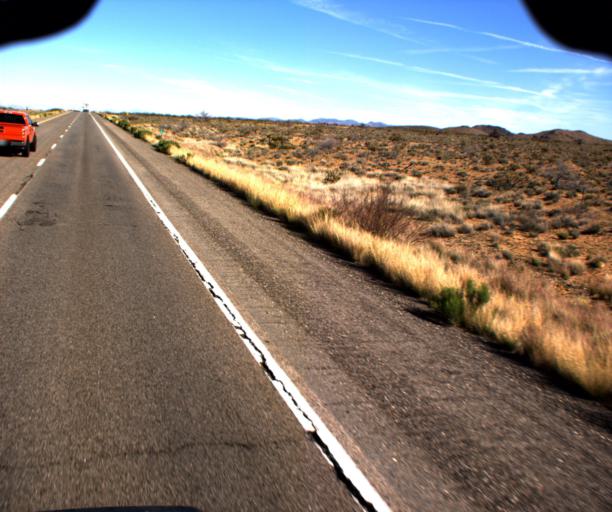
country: US
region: Arizona
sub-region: Mohave County
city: Dolan Springs
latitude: 35.4624
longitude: -114.3057
